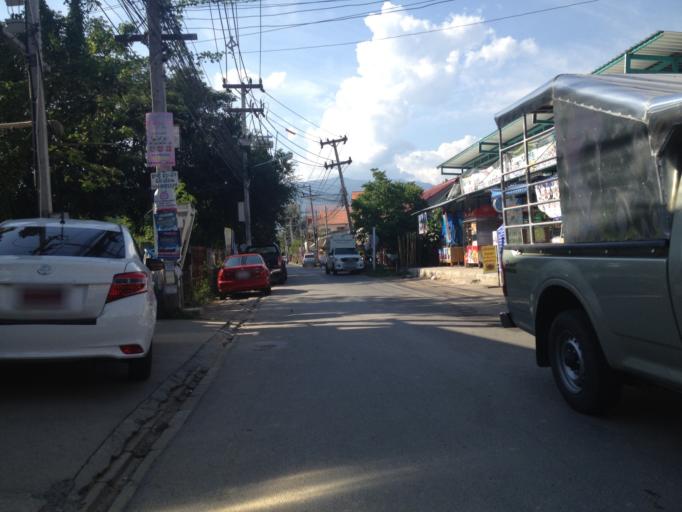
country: TH
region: Chiang Mai
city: Chiang Mai
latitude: 18.7631
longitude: 98.9786
